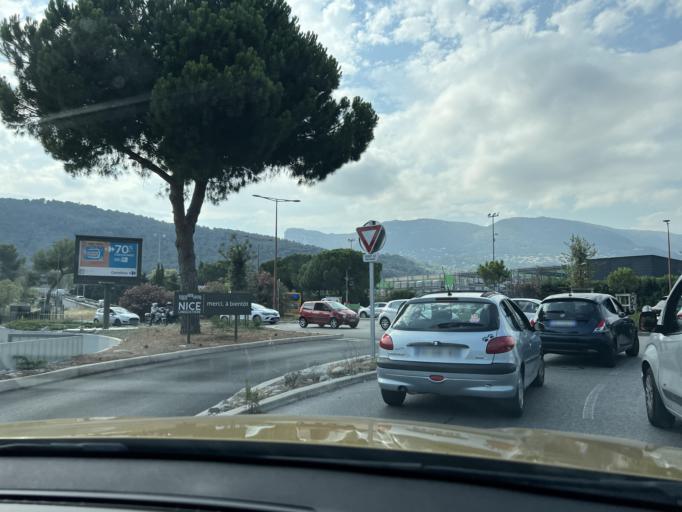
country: FR
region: Provence-Alpes-Cote d'Azur
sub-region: Departement des Alpes-Maritimes
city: Gattieres
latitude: 43.7308
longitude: 7.1883
